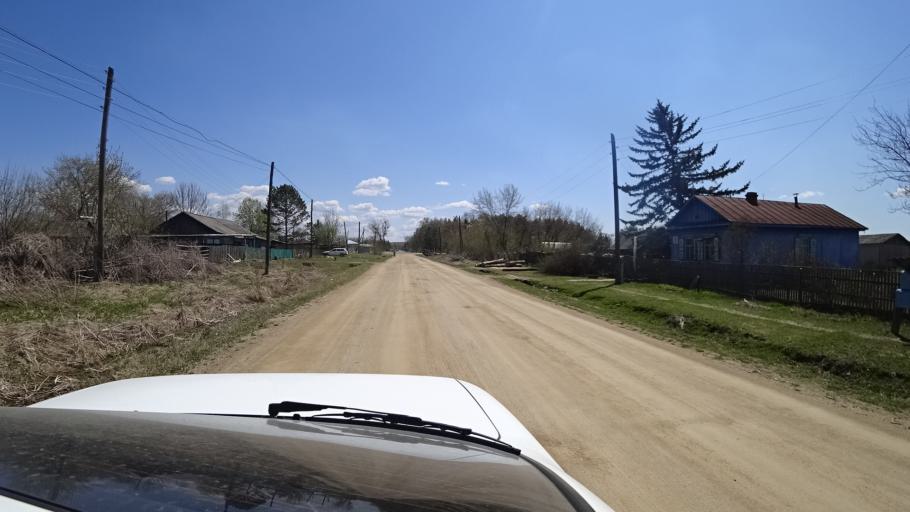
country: RU
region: Primorskiy
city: Dal'nerechensk
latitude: 45.7980
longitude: 133.7670
